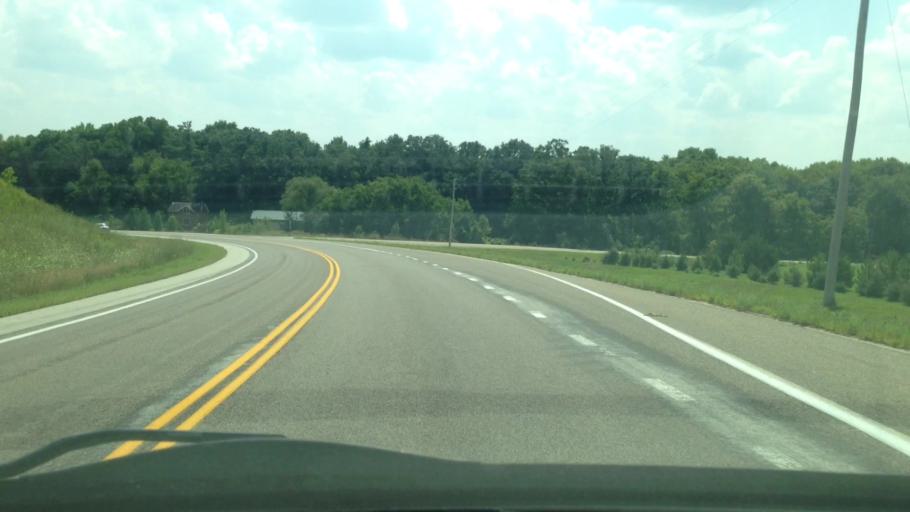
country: US
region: Minnesota
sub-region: Olmsted County
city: Stewartville
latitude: 43.8965
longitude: -92.4112
